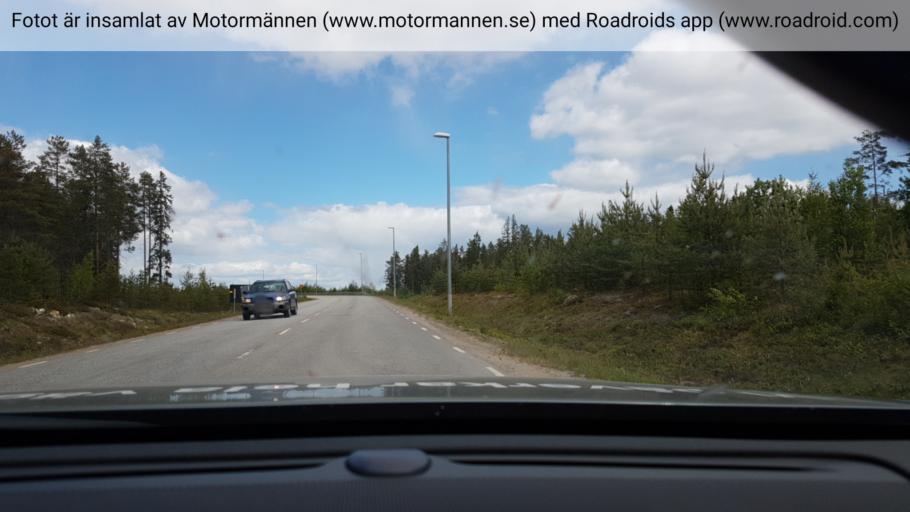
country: SE
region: Vaesterbotten
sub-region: Nordmalings Kommun
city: Nordmaling
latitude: 63.5796
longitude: 19.5317
